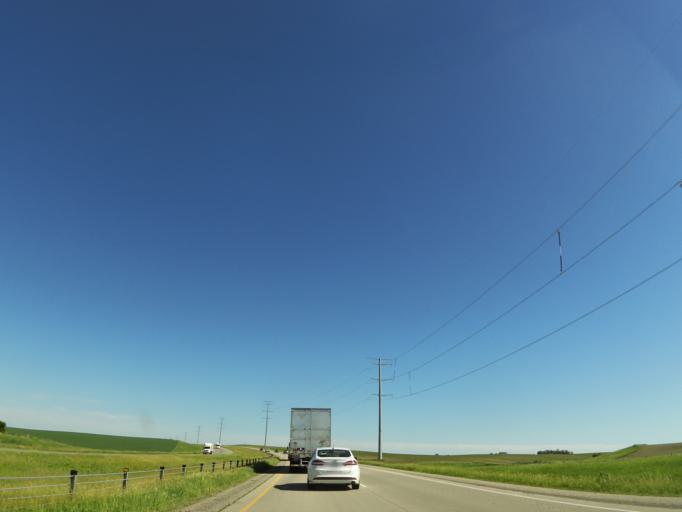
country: US
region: Minnesota
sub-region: Clay County
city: Barnesville
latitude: 46.5212
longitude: -96.2907
